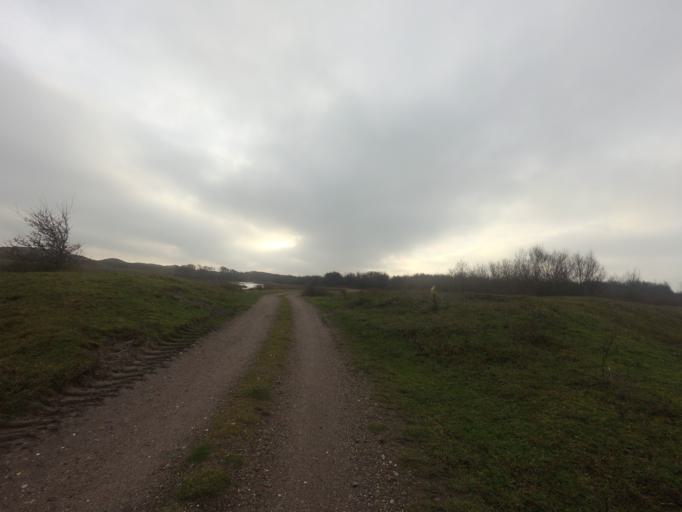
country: NL
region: North Holland
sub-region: Gemeente Texel
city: Den Burg
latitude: 53.1206
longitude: 4.7989
